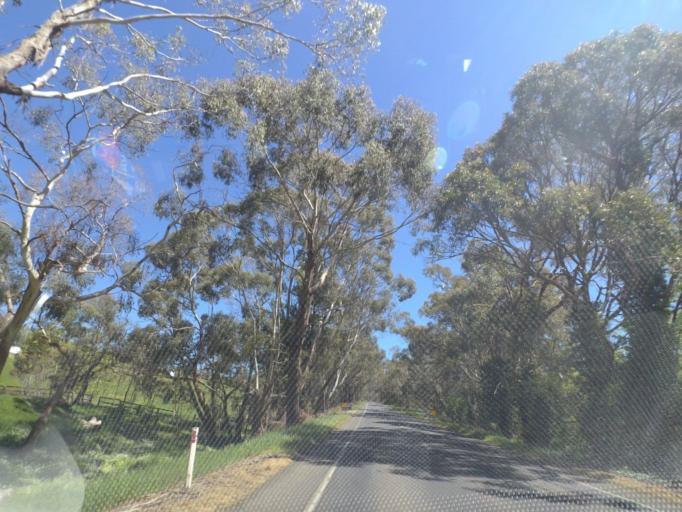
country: AU
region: Victoria
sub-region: Hume
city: Sunbury
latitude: -37.2960
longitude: 144.8018
